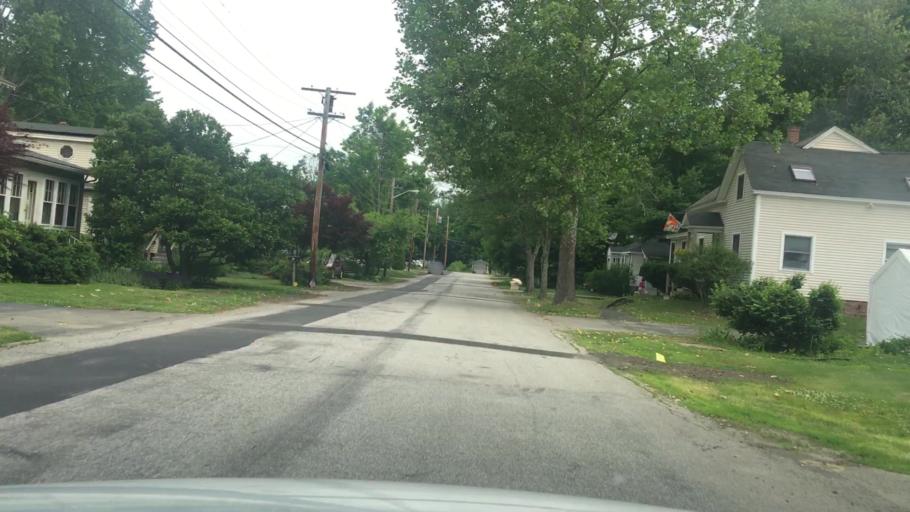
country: US
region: New Hampshire
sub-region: Rockingham County
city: Exeter
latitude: 42.9831
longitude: -70.9657
